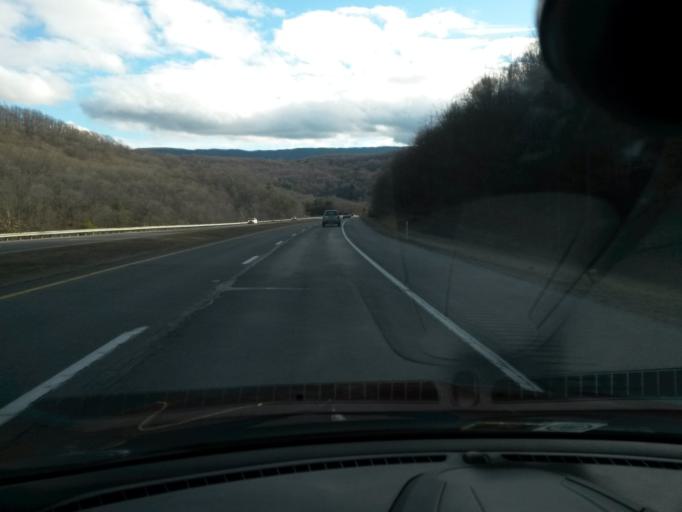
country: US
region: West Virginia
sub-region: Mercer County
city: Athens
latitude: 37.3482
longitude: -81.0138
